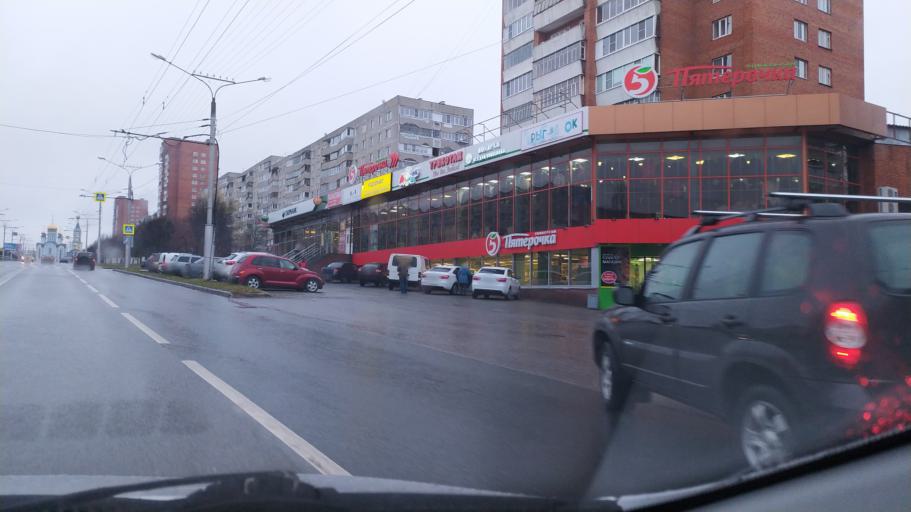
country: RU
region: Chuvashia
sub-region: Cheboksarskiy Rayon
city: Cheboksary
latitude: 56.1462
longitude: 47.1860
